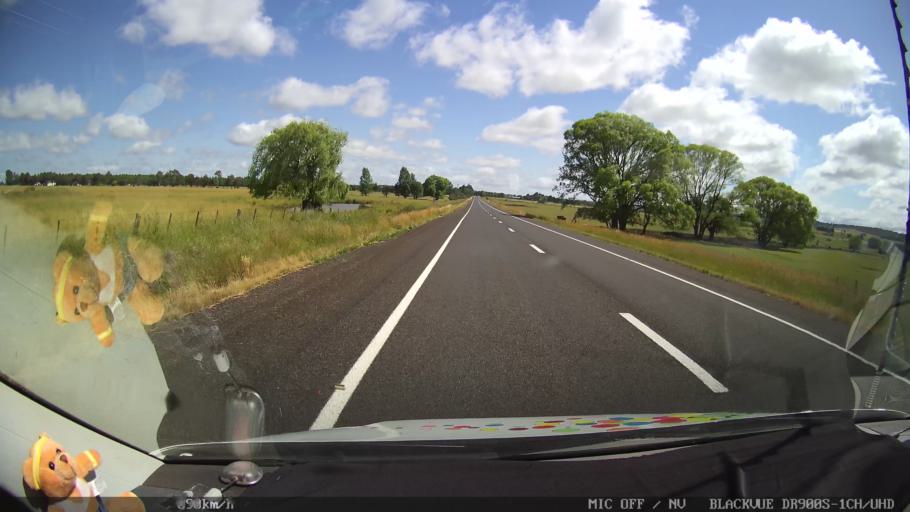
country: AU
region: New South Wales
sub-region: Glen Innes Severn
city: Glen Innes
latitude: -29.8310
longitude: 151.7378
